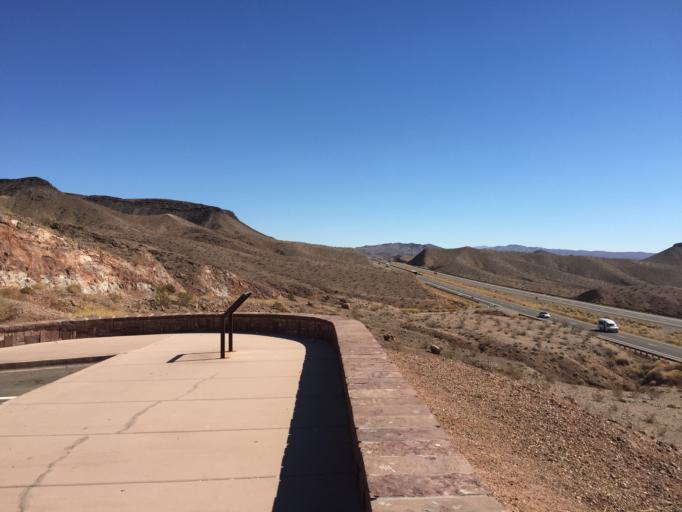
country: US
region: Nevada
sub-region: Clark County
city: Boulder City
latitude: 35.8821
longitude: -114.6153
